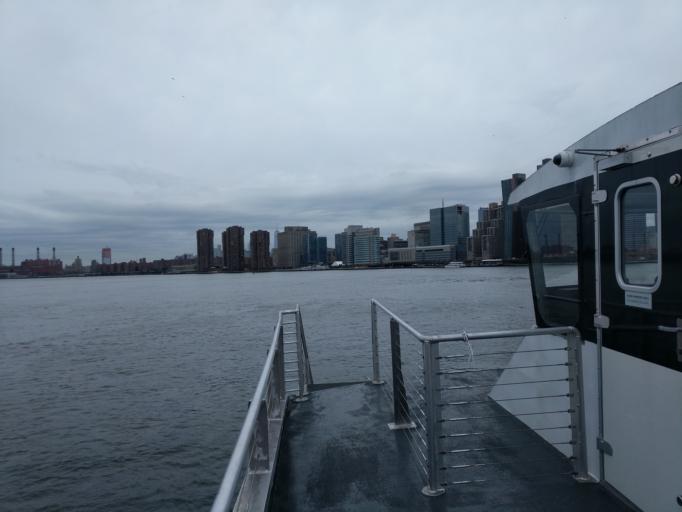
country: US
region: New York
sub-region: Queens County
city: Long Island City
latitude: 40.7462
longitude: -73.9620
